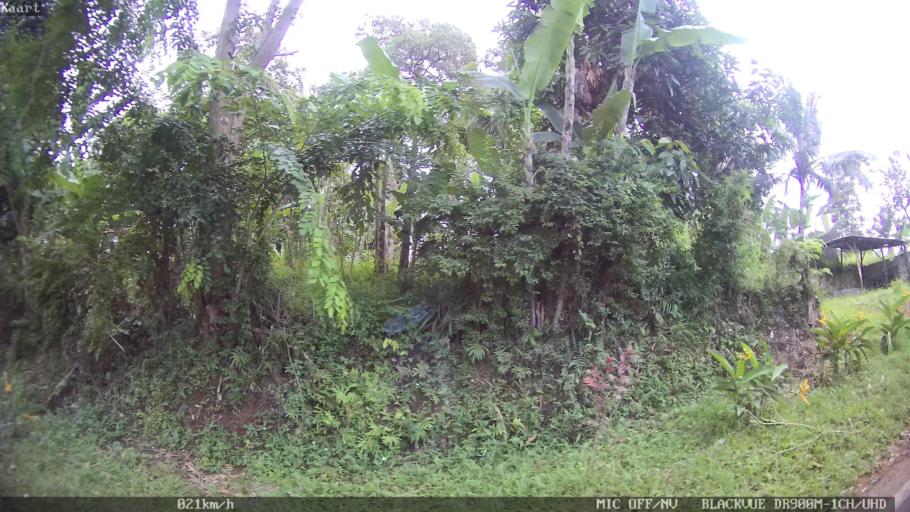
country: ID
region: Lampung
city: Bandarlampung
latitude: -5.4382
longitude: 105.2385
